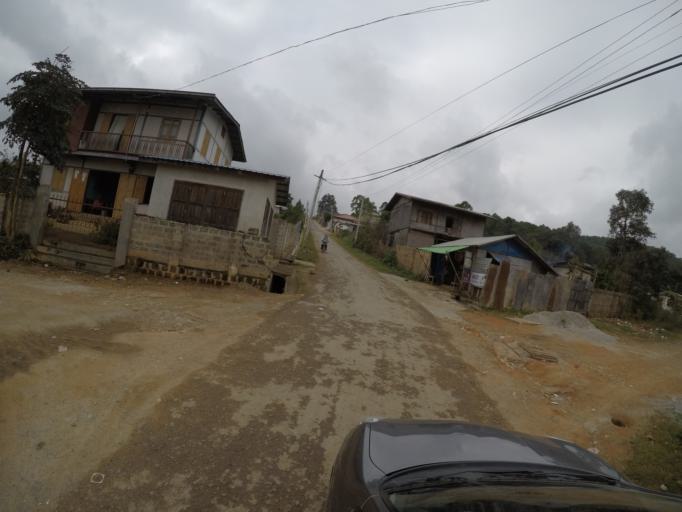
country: MM
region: Shan
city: Taunggyi
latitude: 20.6527
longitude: 96.6261
